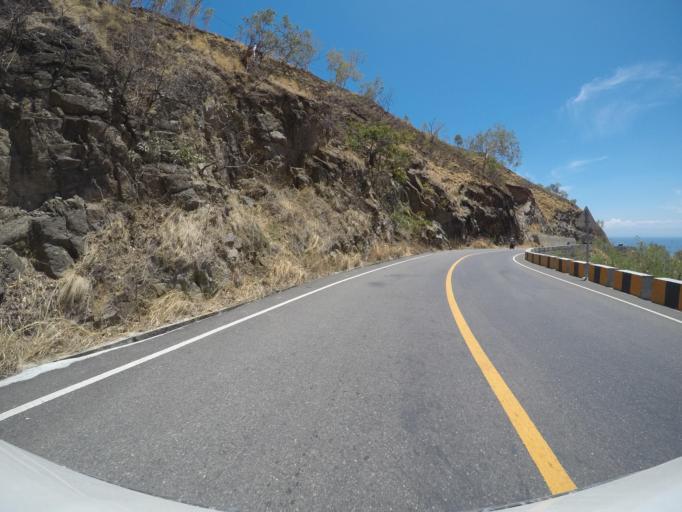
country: TL
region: Manatuto
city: Manatuto
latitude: -8.4861
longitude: 125.9477
